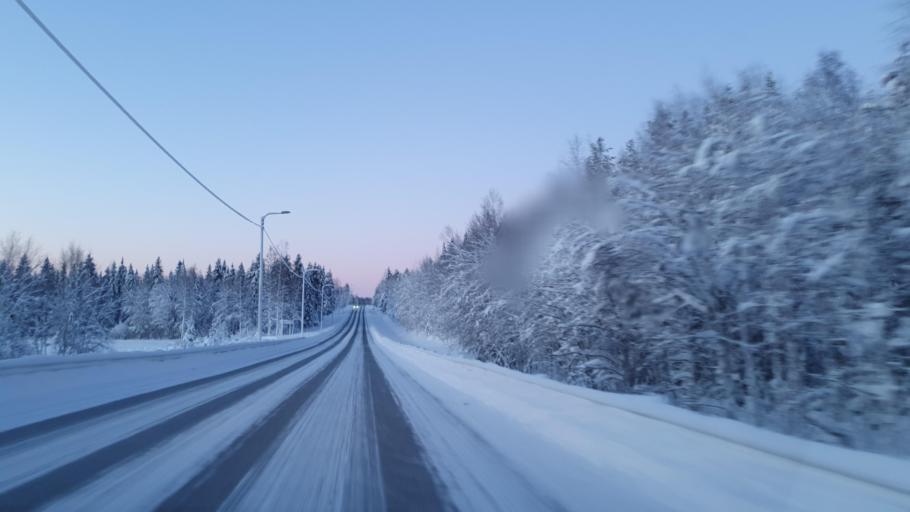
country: FI
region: Lapland
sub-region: Torniolaakso
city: Ylitornio
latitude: 66.2211
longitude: 23.7860
